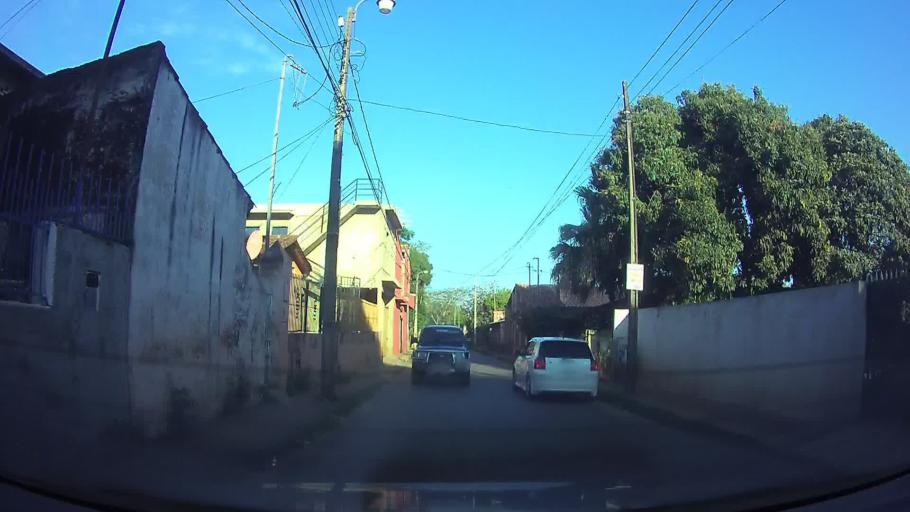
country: PY
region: Central
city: Fernando de la Mora
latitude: -25.3432
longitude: -57.5341
